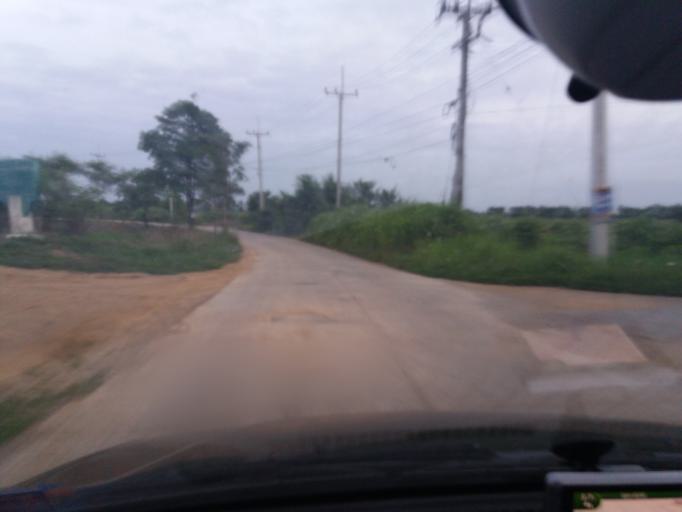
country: TH
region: Suphan Buri
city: Ban Sam Chuk
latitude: 14.7313
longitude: 100.0811
